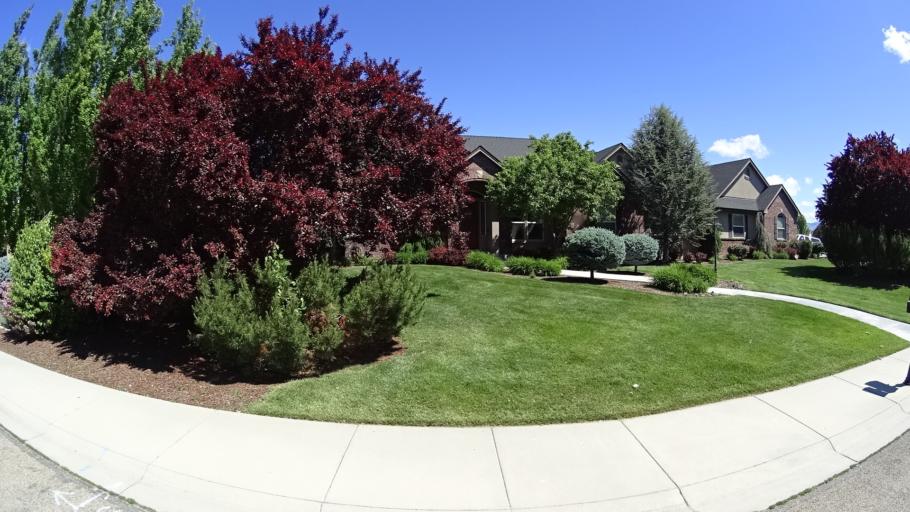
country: US
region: Idaho
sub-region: Ada County
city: Eagle
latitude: 43.6680
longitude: -116.3809
